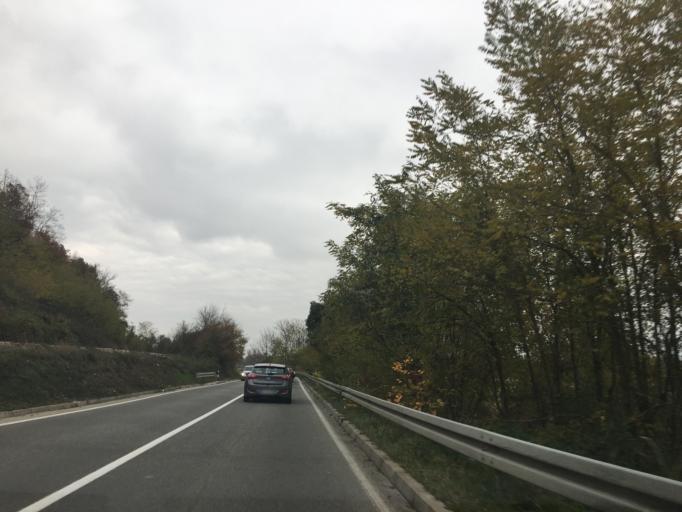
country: RS
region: Central Serbia
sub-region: Raski Okrug
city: Kraljevo
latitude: 43.7126
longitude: 20.7858
